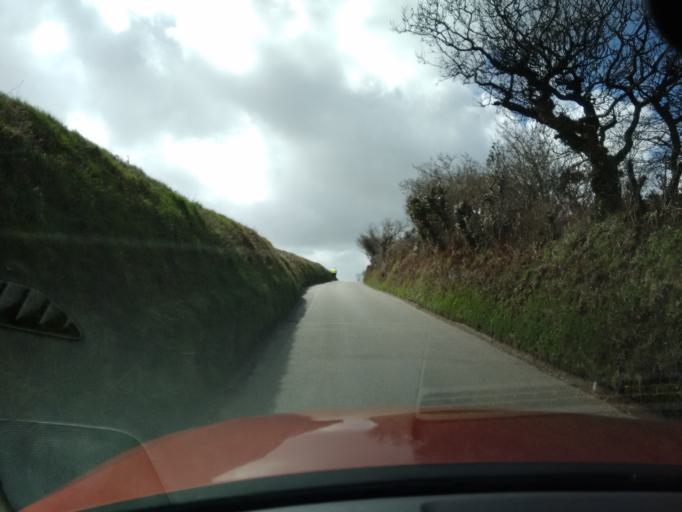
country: GB
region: England
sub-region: Cornwall
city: Liskeard
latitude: 50.4939
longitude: -4.4848
